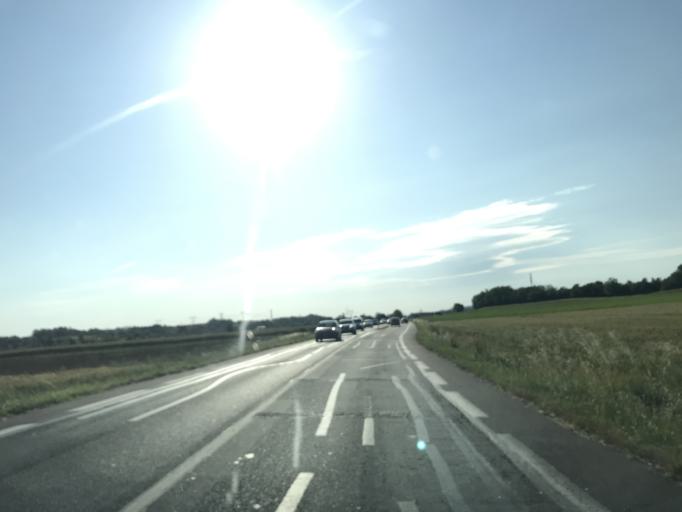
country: FR
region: Rhone-Alpes
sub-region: Departement du Rhone
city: Mions
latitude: 45.6531
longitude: 4.9378
